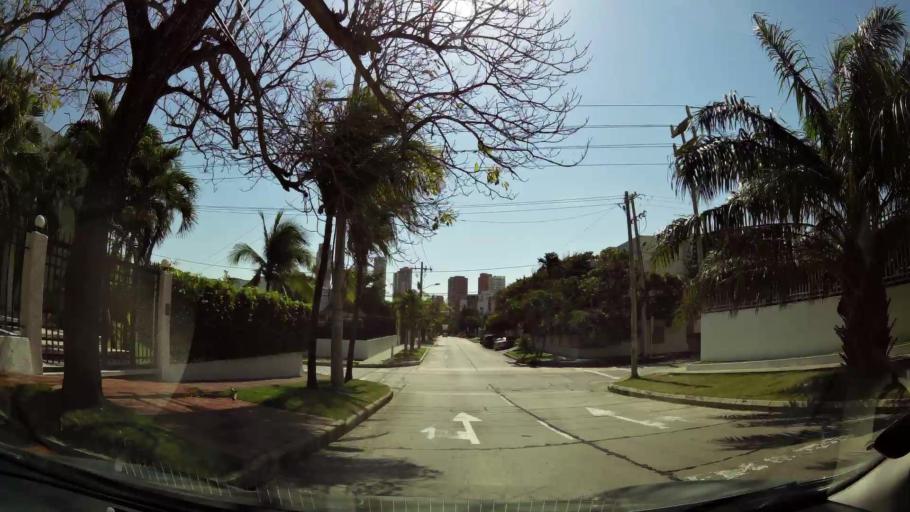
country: CO
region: Atlantico
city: Barranquilla
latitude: 11.0123
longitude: -74.8169
